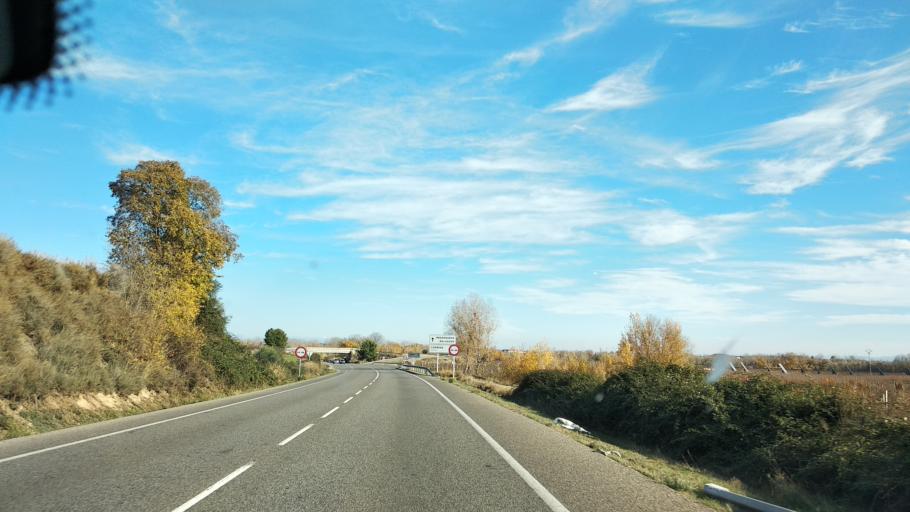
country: ES
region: Catalonia
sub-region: Provincia de Lleida
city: Corbins
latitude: 41.6826
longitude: 0.6924
